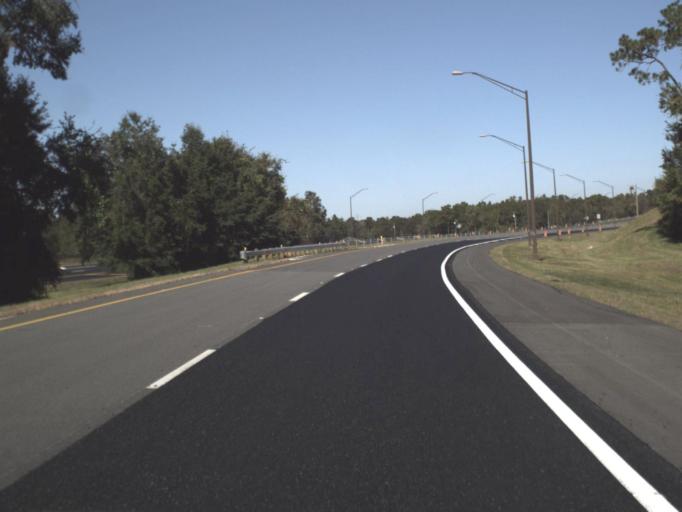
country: US
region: Florida
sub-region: Citrus County
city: Sugarmill Woods
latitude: 28.6478
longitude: -82.4923
